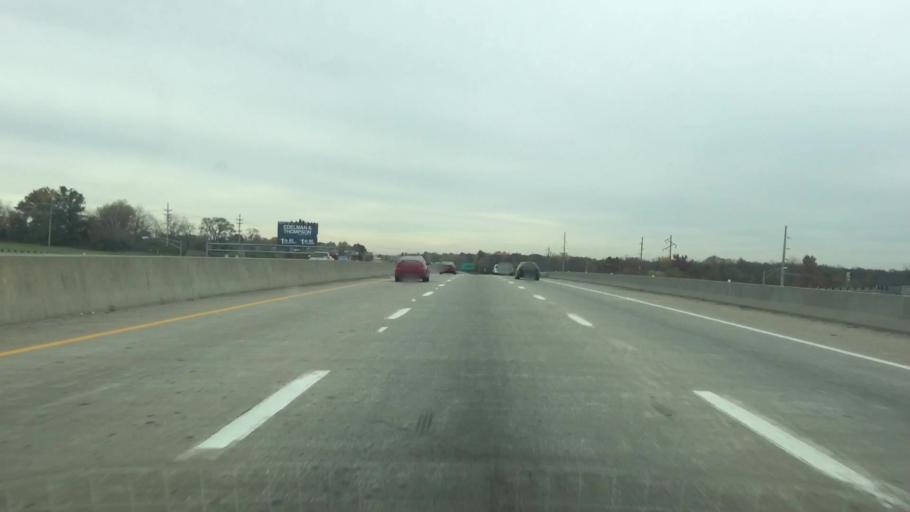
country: US
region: Missouri
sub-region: Jackson County
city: Grandview
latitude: 38.8576
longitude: -94.5281
